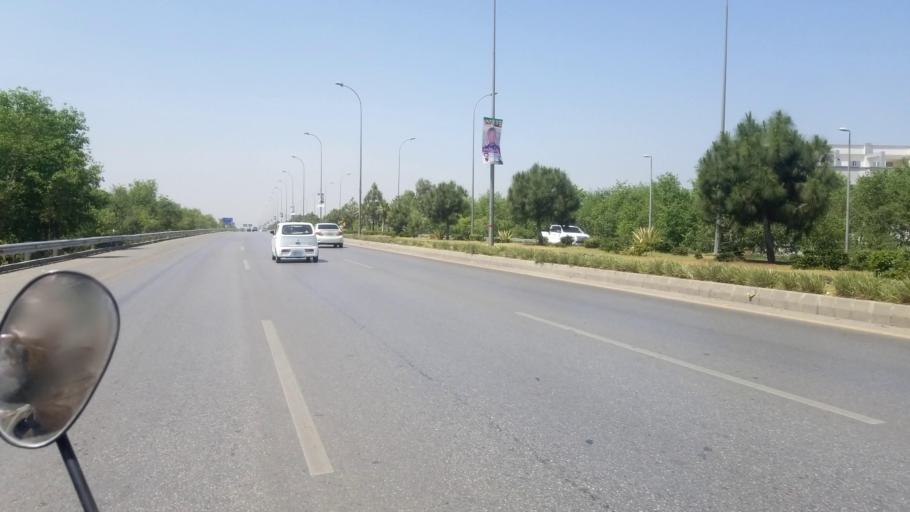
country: PK
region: Khyber Pakhtunkhwa
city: Peshawar
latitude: 34.0280
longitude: 71.6561
